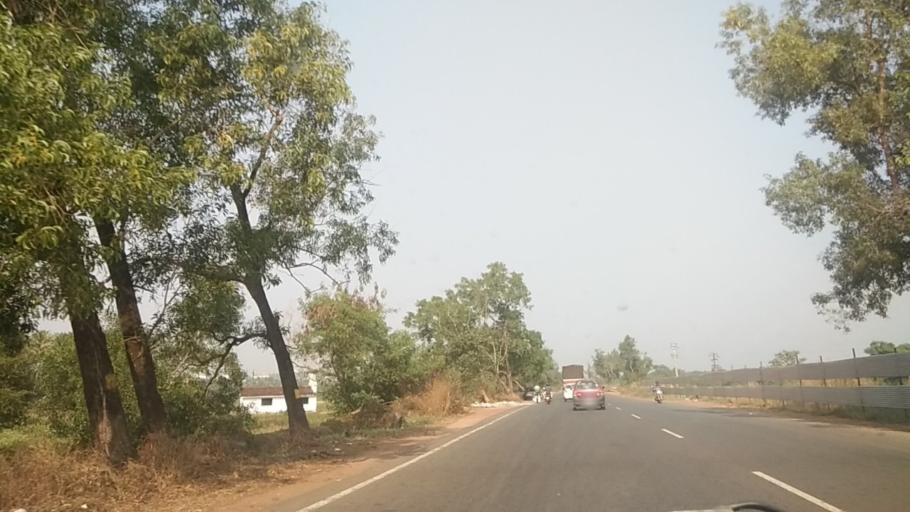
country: IN
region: Goa
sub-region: North Goa
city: Guirim
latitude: 15.5762
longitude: 73.8089
